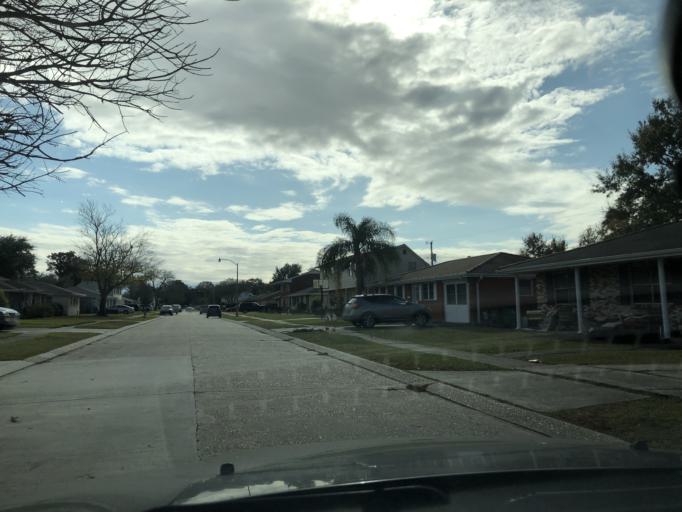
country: US
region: Louisiana
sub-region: Jefferson Parish
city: Metairie Terrace
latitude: 29.9875
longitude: -90.1669
